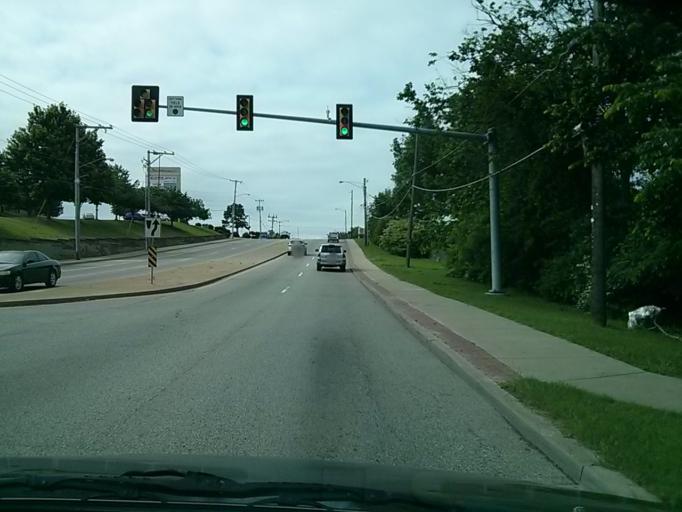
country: US
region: Oklahoma
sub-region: Tulsa County
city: Tulsa
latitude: 36.1068
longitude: -95.9224
